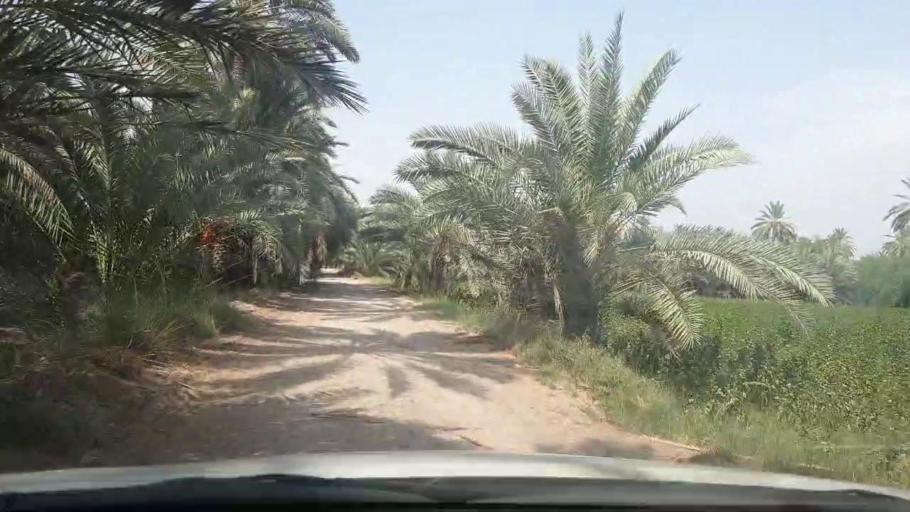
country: PK
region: Sindh
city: Rohri
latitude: 27.5899
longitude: 68.8551
